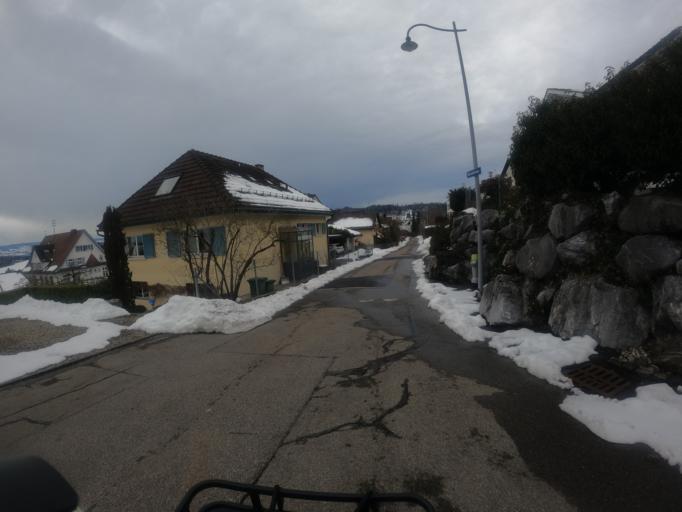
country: CH
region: Zurich
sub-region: Bezirk Affoltern
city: Hedingen
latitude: 47.3014
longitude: 8.4504
